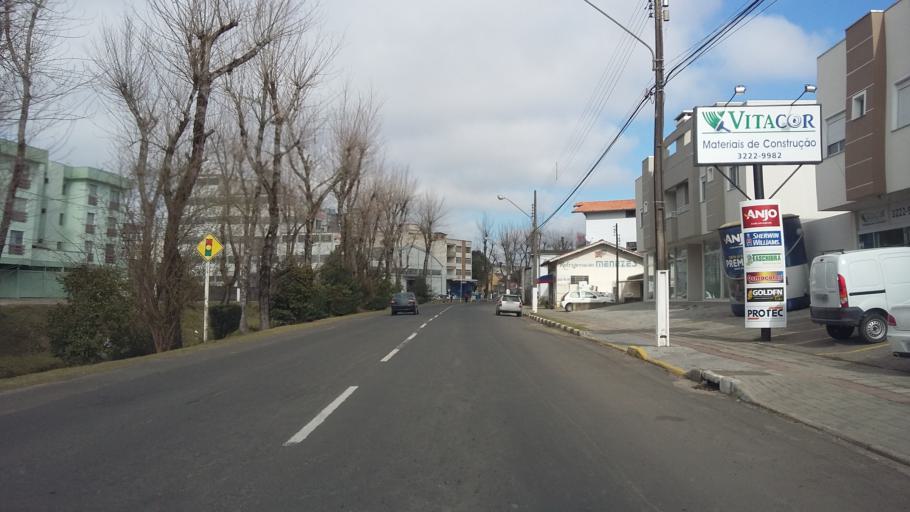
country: BR
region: Santa Catarina
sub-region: Lages
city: Lages
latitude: -27.8096
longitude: -50.3257
